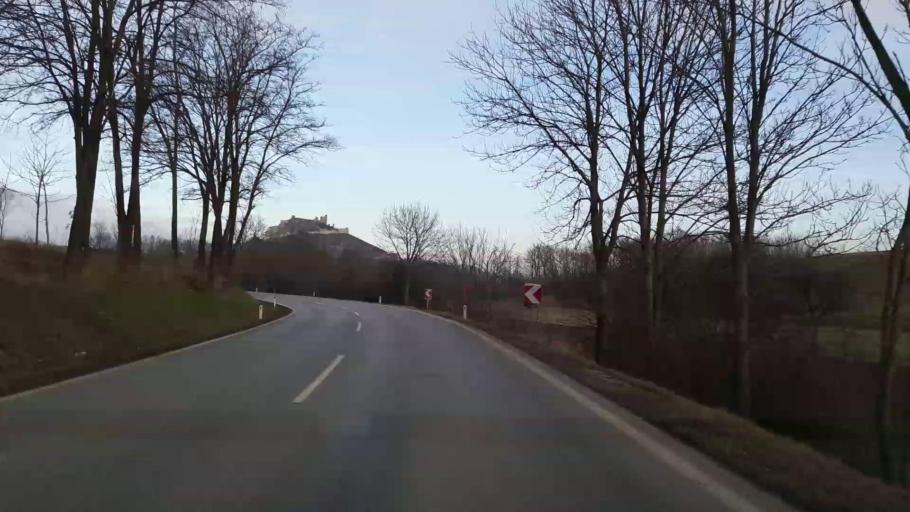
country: AT
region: Lower Austria
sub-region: Politischer Bezirk Mistelbach
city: Staatz
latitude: 48.6657
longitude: 16.4933
